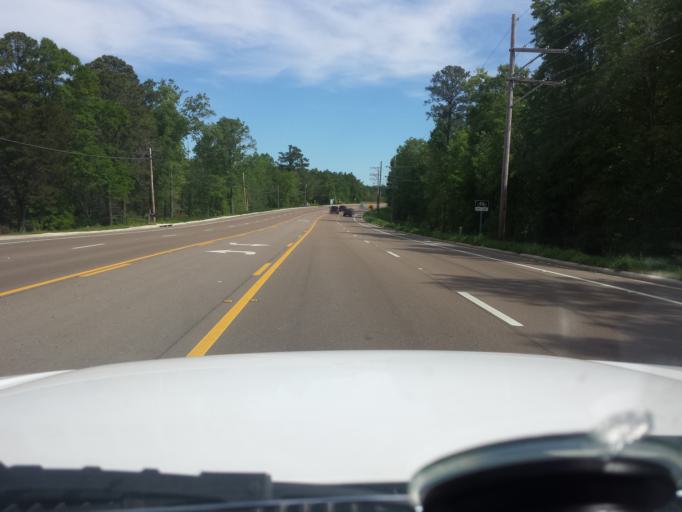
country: US
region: Mississippi
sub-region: Rankin County
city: Flowood
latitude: 32.3643
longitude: -90.0559
